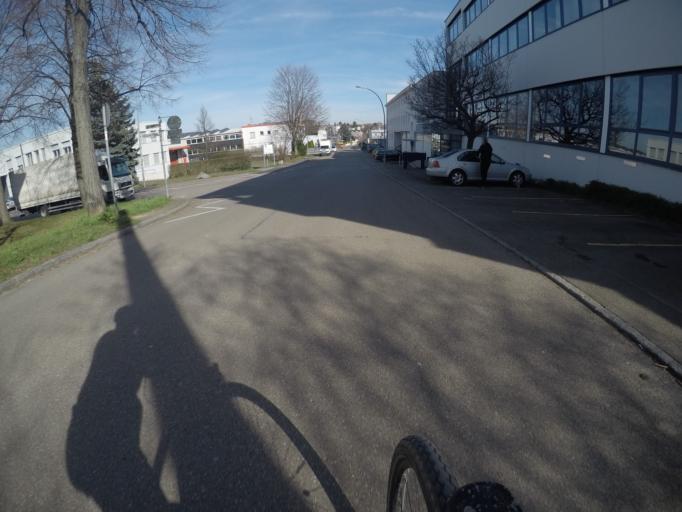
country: DE
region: Baden-Wuerttemberg
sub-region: Regierungsbezirk Stuttgart
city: Stuttgart Muehlhausen
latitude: 48.8426
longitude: 9.2532
